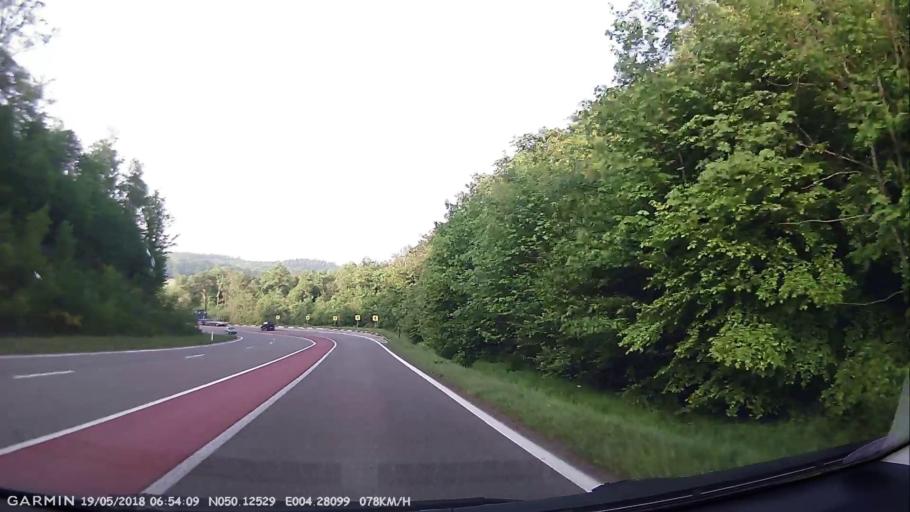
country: BE
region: Wallonia
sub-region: Province du Hainaut
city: Froidchapelle
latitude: 50.1251
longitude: 4.2808
